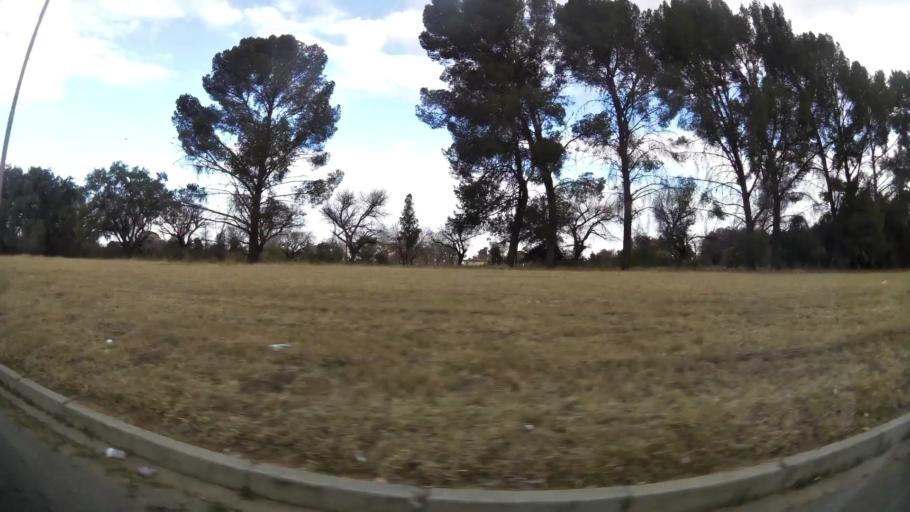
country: ZA
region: Orange Free State
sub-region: Lejweleputswa District Municipality
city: Welkom
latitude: -27.9965
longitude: 26.7136
